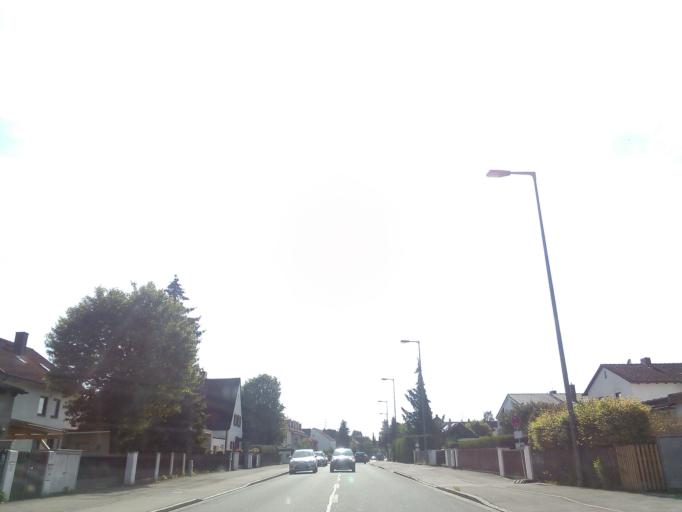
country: DE
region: Bavaria
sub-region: Upper Bavaria
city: Pasing
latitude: 48.1637
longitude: 11.4421
